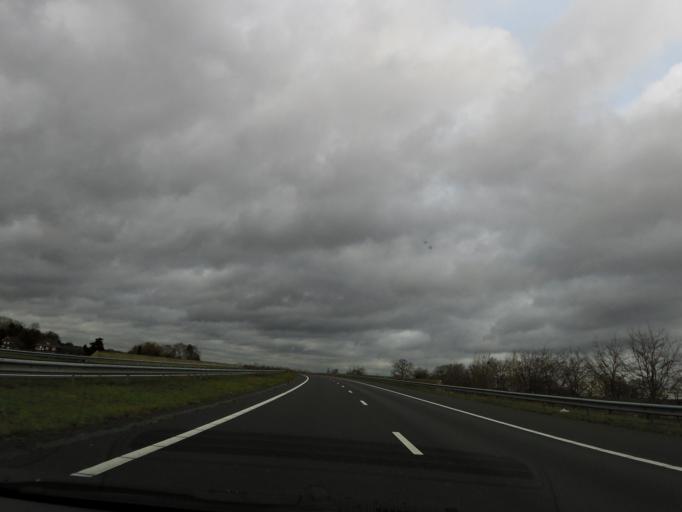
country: NL
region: Limburg
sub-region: Gemeente Beesel
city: Offenbeek
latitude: 51.2767
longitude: 6.1005
